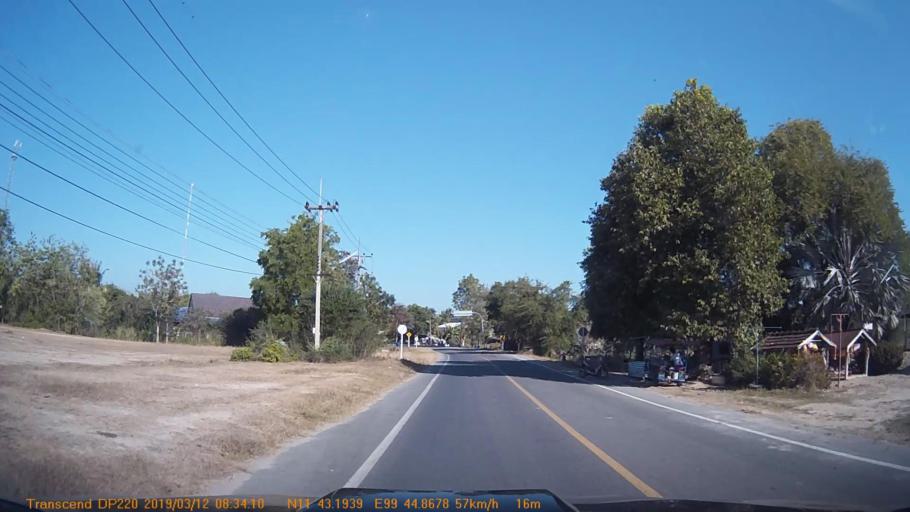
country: TH
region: Prachuap Khiri Khan
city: Prachuap Khiri Khan
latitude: 11.7201
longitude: 99.7476
